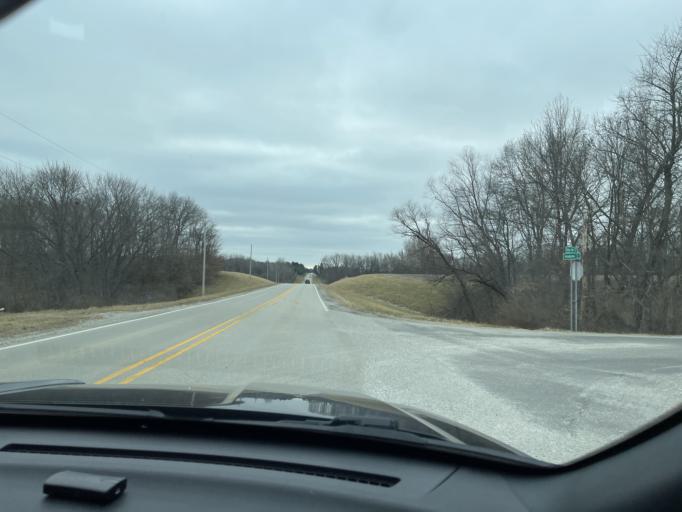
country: US
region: Illinois
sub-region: Sangamon County
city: Leland Grove
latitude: 39.8147
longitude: -89.7396
